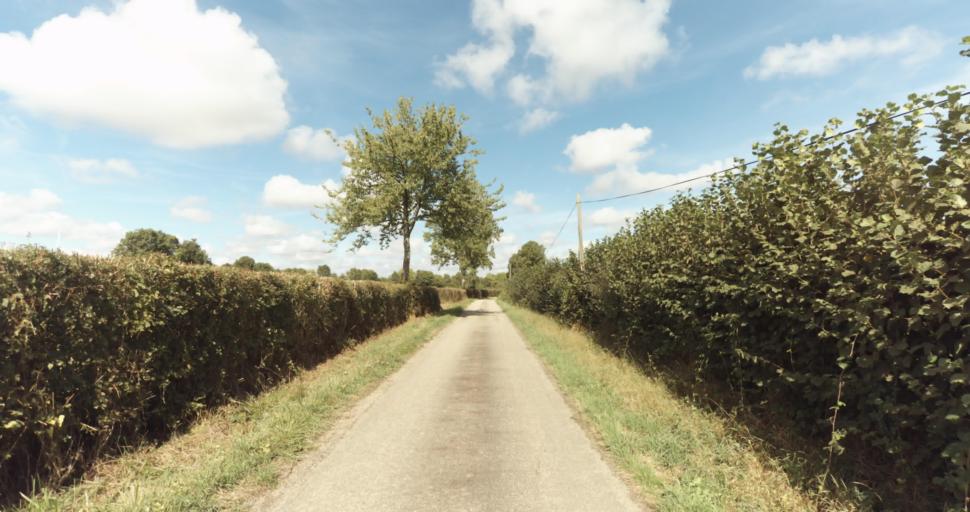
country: FR
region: Lower Normandy
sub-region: Departement du Calvados
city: Orbec
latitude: 48.9680
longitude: 0.3805
